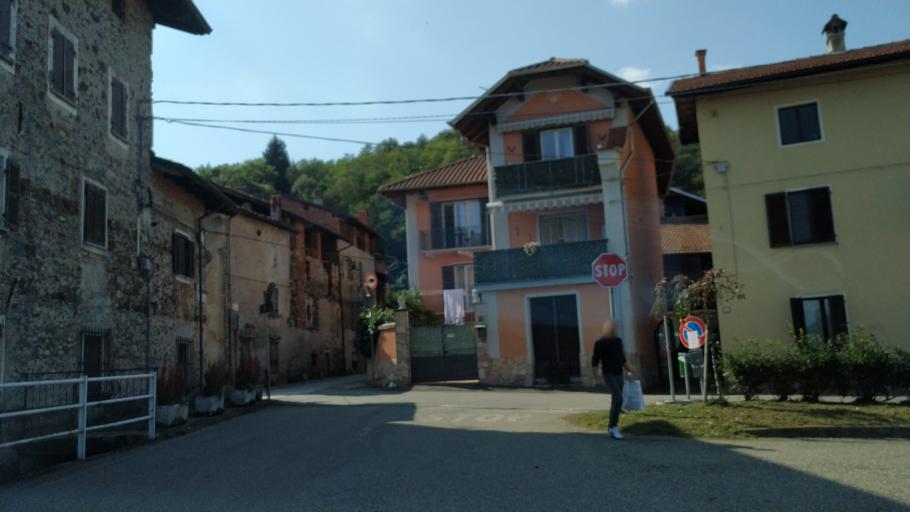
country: IT
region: Piedmont
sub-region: Provincia di Vercelli
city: Serravalle Sesia
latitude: 45.6769
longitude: 8.3132
